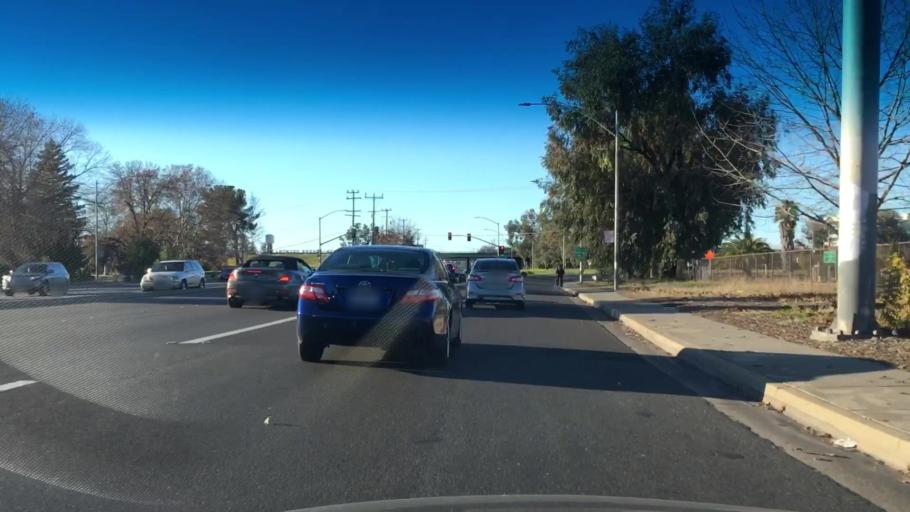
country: US
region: California
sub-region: Sacramento County
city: Arden-Arcade
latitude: 38.6019
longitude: -121.4314
